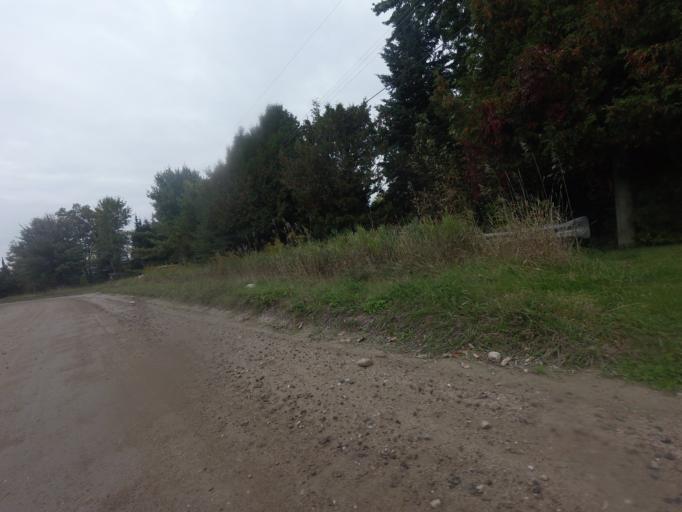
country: CA
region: Quebec
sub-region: Outaouais
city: Maniwaki
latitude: 46.0304
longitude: -75.9452
